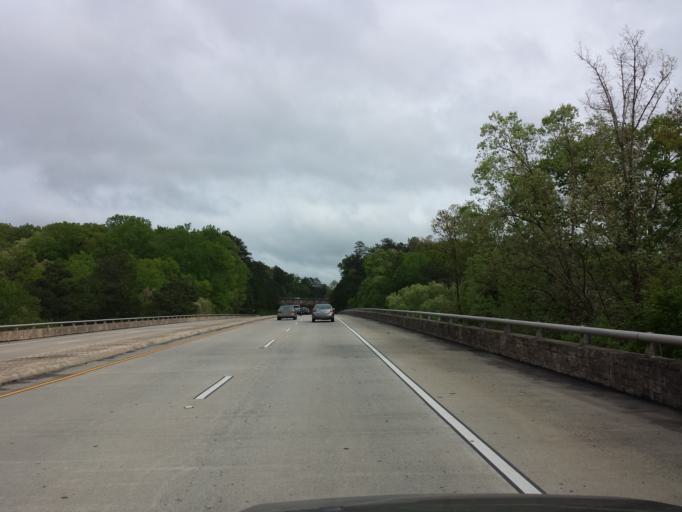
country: US
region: Georgia
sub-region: Cobb County
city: Mableton
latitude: 33.8543
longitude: -84.5601
